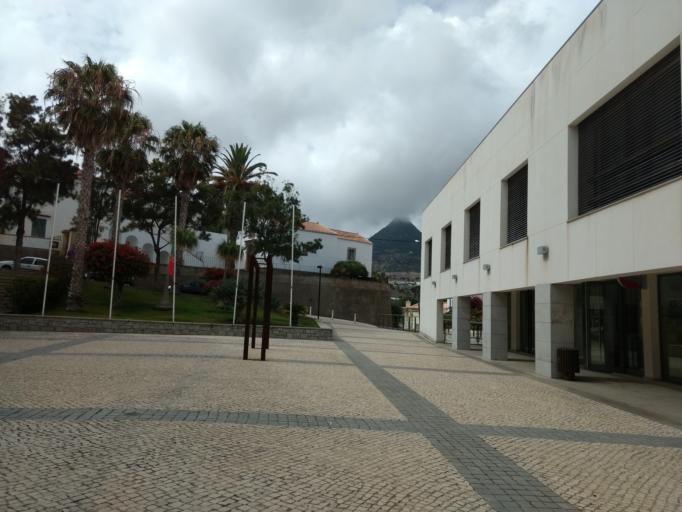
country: PT
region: Madeira
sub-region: Porto Santo
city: Vila de Porto Santo
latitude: 33.0597
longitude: -16.3351
